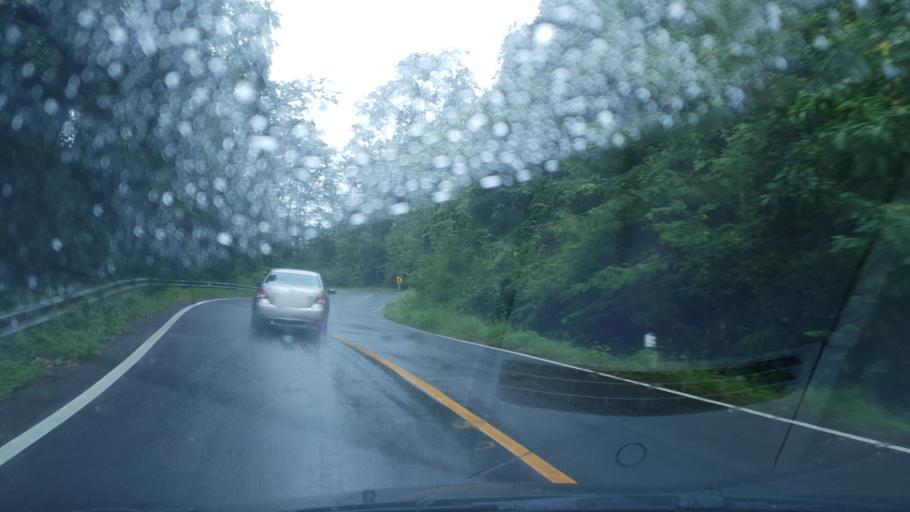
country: TH
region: Mae Hong Son
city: Khun Yuam
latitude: 18.6705
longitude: 97.9270
